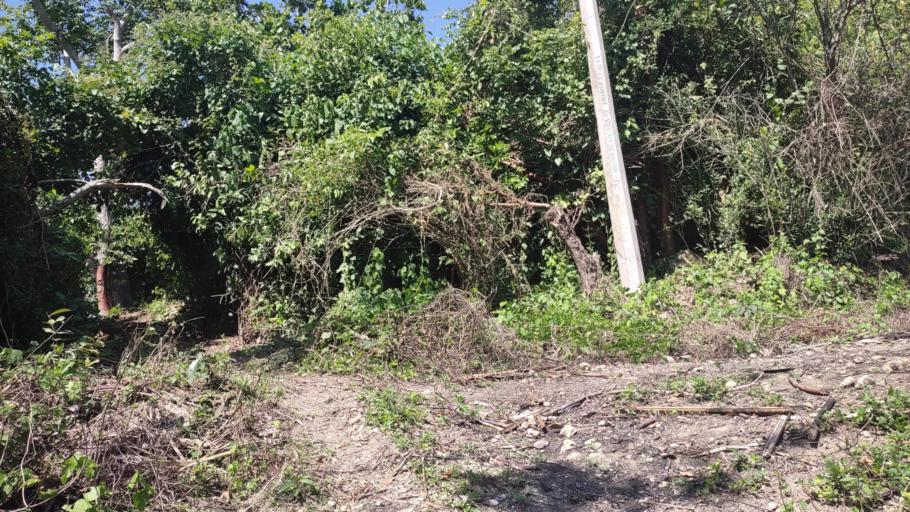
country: MX
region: Veracruz
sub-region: Papantla
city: Polutla
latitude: 20.5035
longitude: -97.2181
